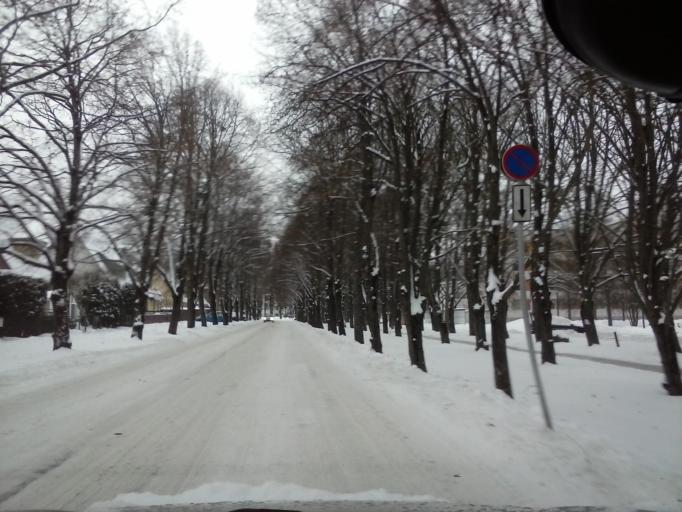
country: EE
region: Tartu
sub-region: Tartu linn
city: Tartu
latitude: 58.3645
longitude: 26.6910
